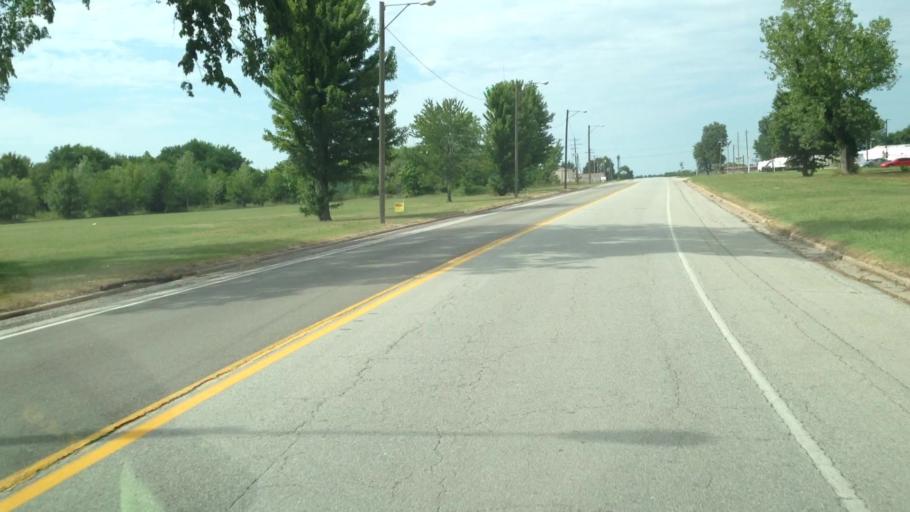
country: US
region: Kansas
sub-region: Labette County
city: Chetopa
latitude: 37.0392
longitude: -95.1002
